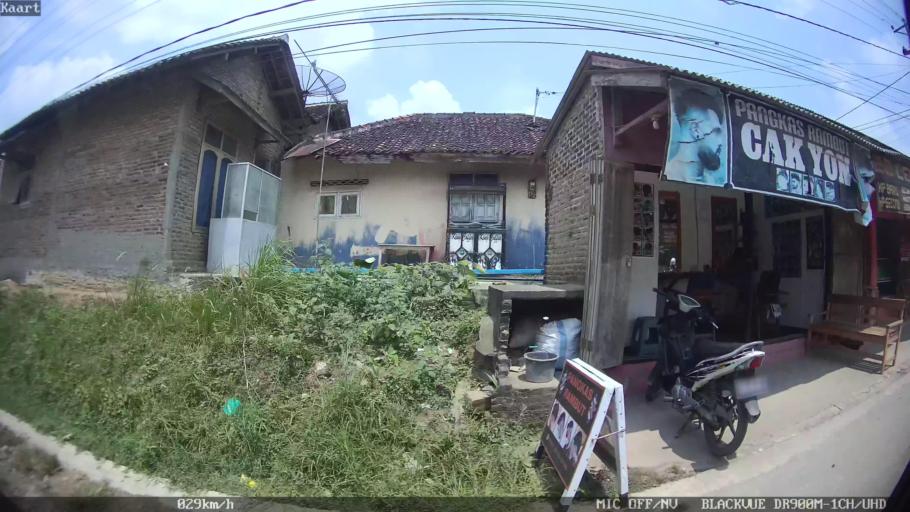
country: ID
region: Lampung
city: Pringsewu
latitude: -5.3412
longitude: 104.9749
